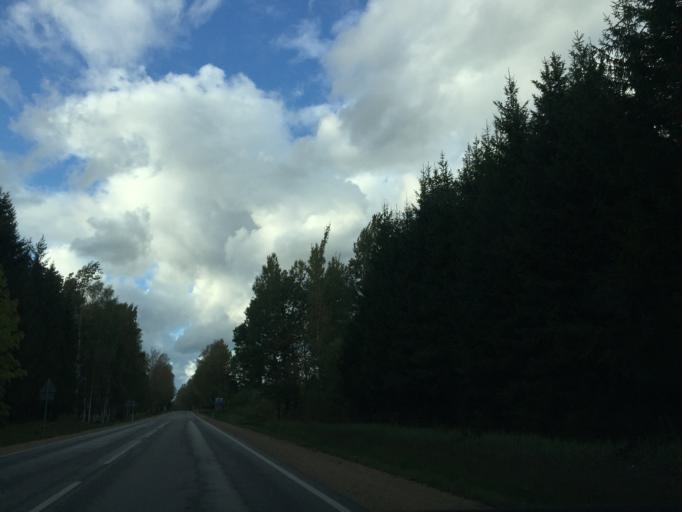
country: LV
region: Ligatne
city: Ligatne
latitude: 57.1770
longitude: 25.0396
